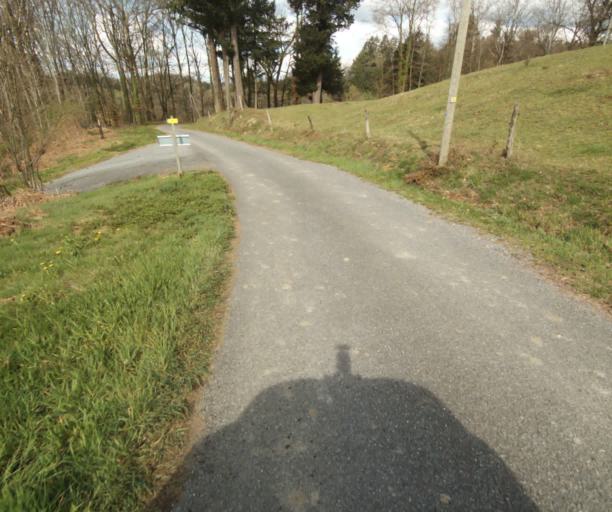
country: FR
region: Limousin
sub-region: Departement de la Correze
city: Correze
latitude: 45.3540
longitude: 1.8826
